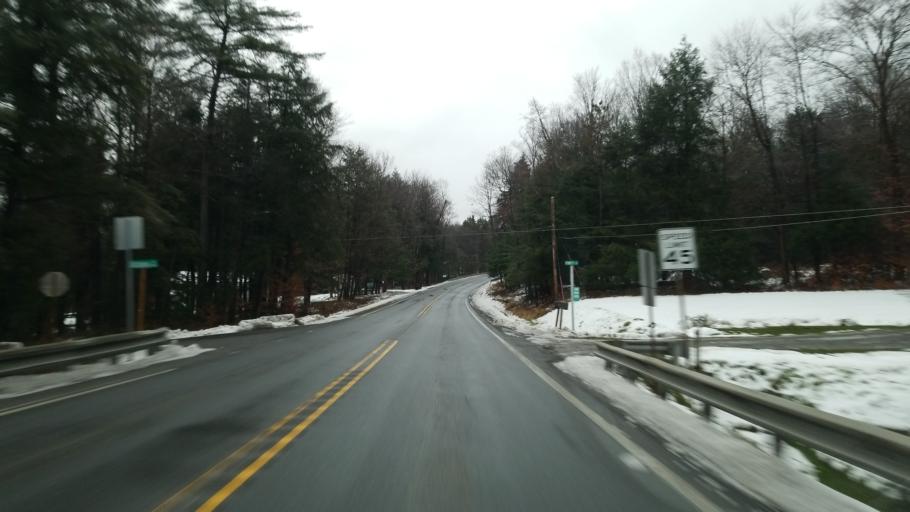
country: US
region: Pennsylvania
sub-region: Clearfield County
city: DuBois
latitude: 41.0780
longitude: -78.6668
